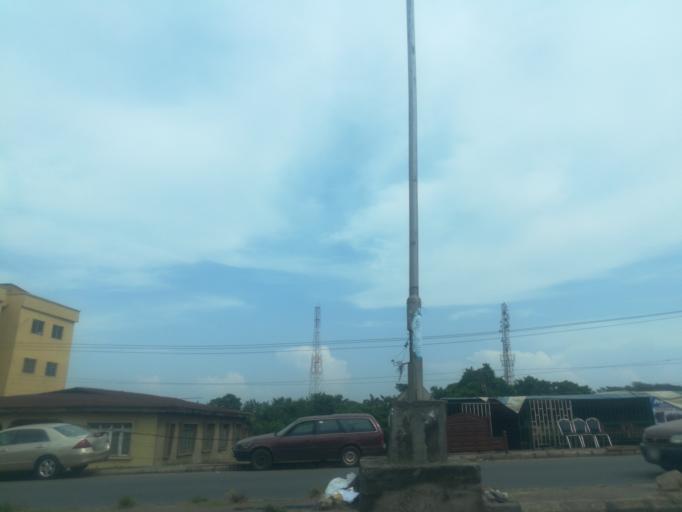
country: NG
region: Oyo
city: Ibadan
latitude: 7.4165
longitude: 3.8954
